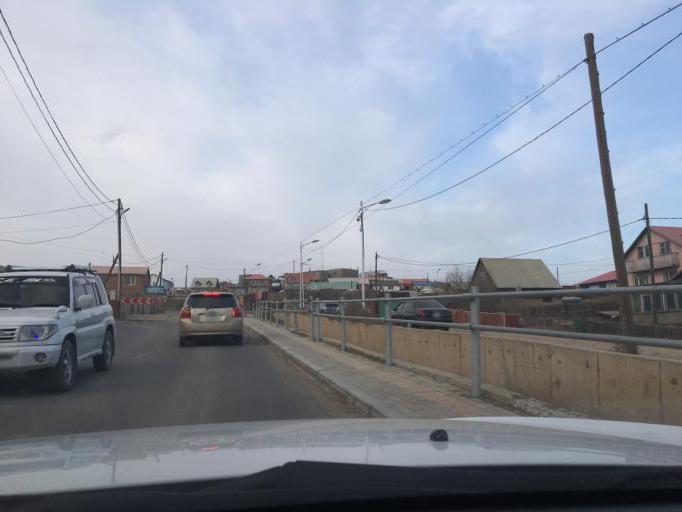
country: MN
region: Ulaanbaatar
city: Ulaanbaatar
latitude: 47.9218
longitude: 106.8525
